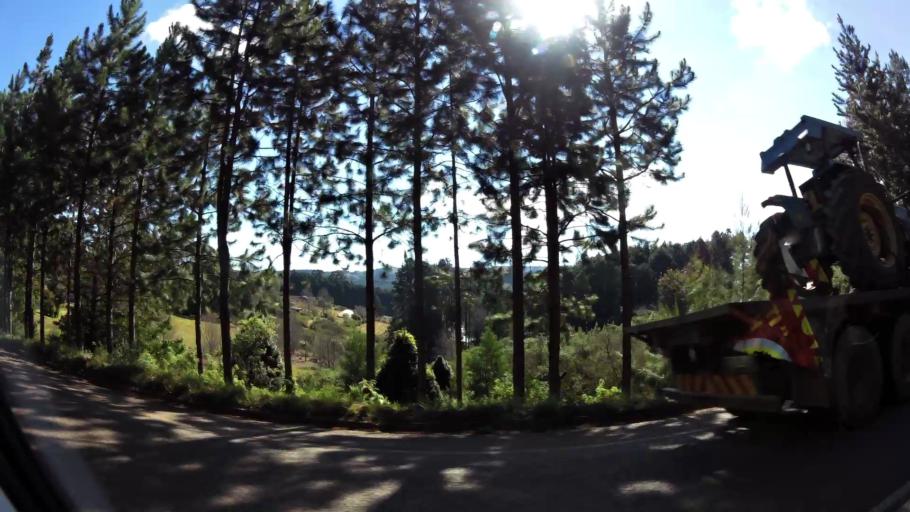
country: ZA
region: Limpopo
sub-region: Capricorn District Municipality
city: Mankoeng
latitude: -23.9065
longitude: 29.9864
